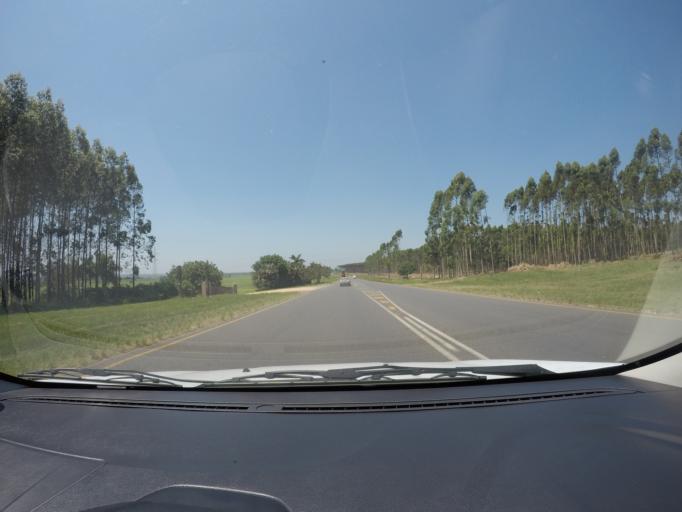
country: ZA
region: KwaZulu-Natal
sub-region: uThungulu District Municipality
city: eSikhawini
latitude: -28.8185
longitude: 31.9516
